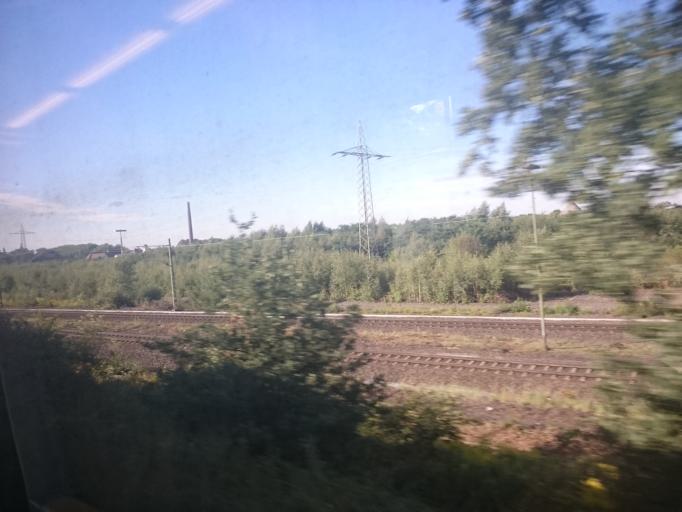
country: DE
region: North Rhine-Westphalia
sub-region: Regierungsbezirk Dusseldorf
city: Duisburg
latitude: 51.4056
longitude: 6.8000
